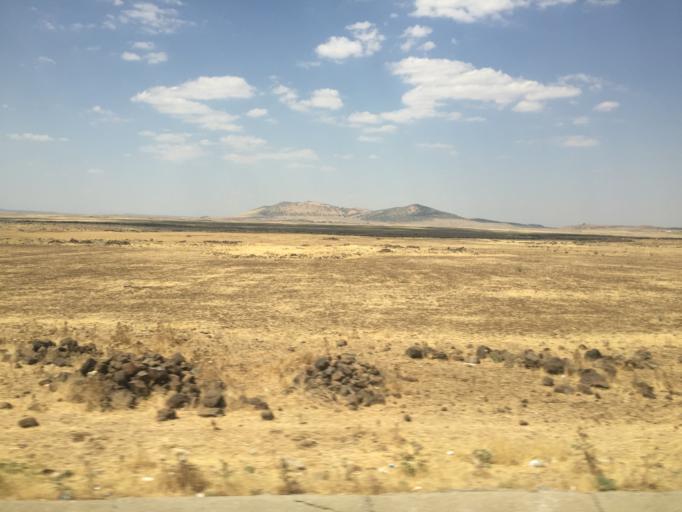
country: TR
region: Sanliurfa
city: Karacadag
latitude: 37.8455
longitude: 39.7065
